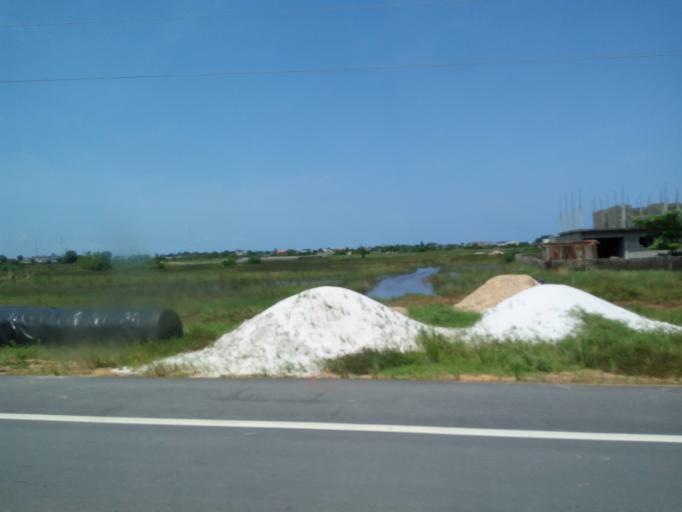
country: CI
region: Sud-Comoe
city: Grand-Bassam
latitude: 5.2285
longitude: -3.7474
